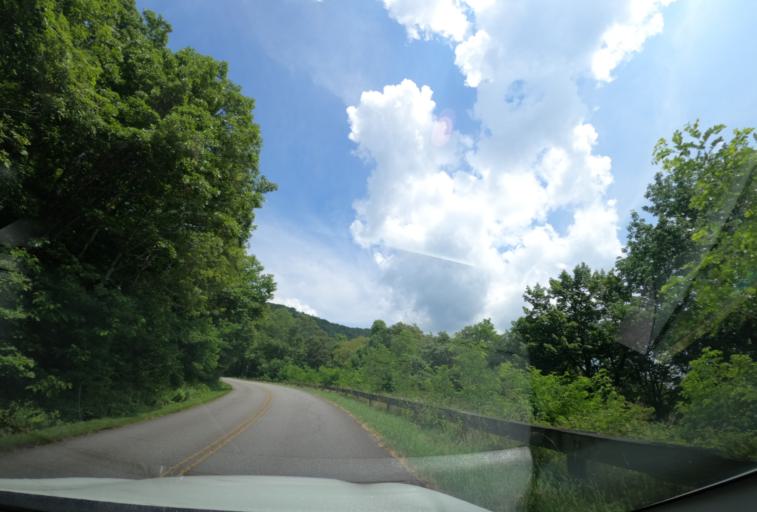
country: US
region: North Carolina
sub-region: Transylvania County
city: Brevard
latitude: 35.3533
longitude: -82.7991
